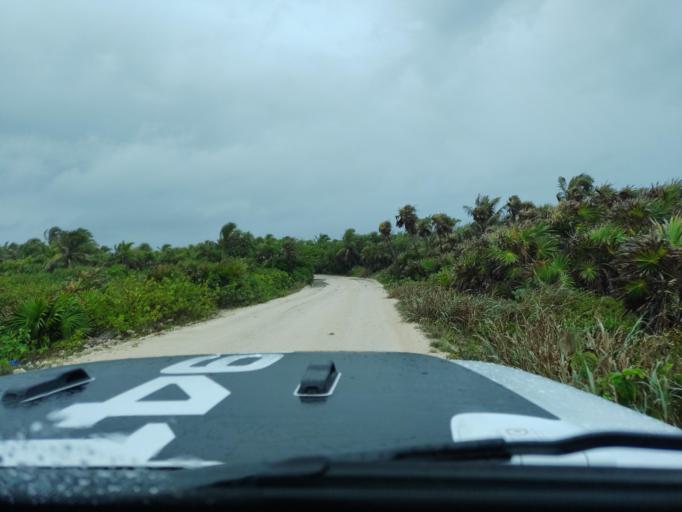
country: MX
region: Quintana Roo
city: Tulum
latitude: 19.9906
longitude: -87.4646
